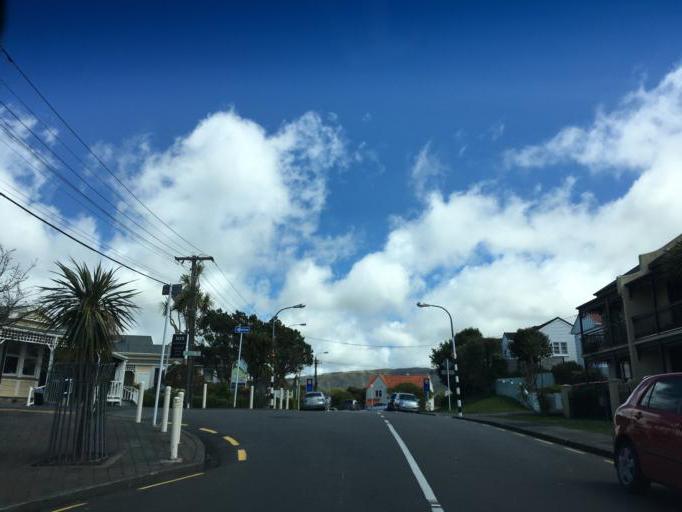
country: NZ
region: Wellington
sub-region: Wellington City
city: Wellington
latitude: -41.2463
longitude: 174.7910
